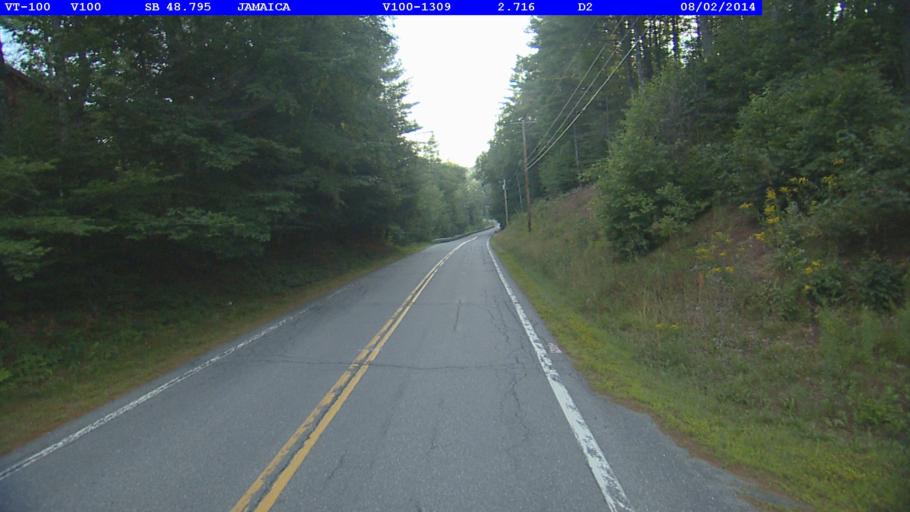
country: US
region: Vermont
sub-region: Windham County
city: Newfane
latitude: 43.0704
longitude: -72.7477
